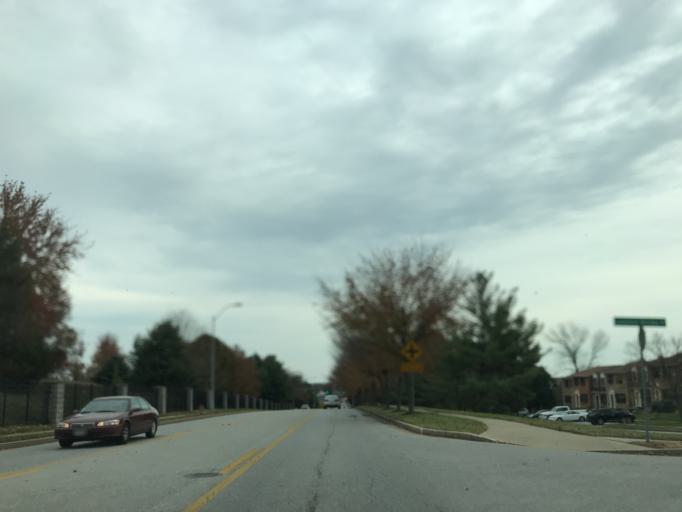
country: US
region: Maryland
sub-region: Baltimore County
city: Charlestown
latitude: 39.2677
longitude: -76.7045
